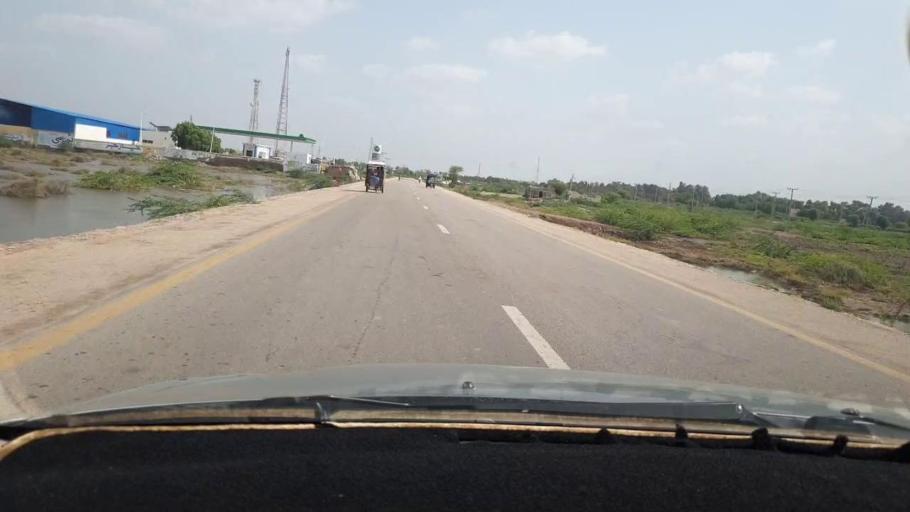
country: PK
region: Sindh
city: Digri
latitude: 25.0798
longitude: 69.2066
